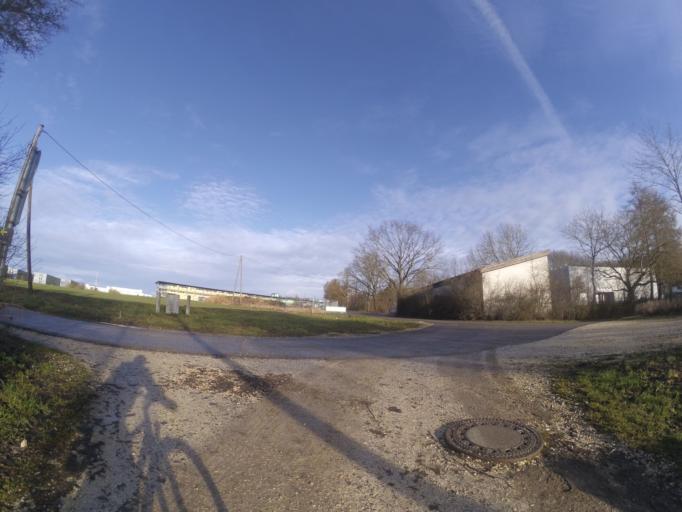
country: DE
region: Baden-Wuerttemberg
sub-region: Tuebingen Region
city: Ulm
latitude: 48.4169
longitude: 9.9468
